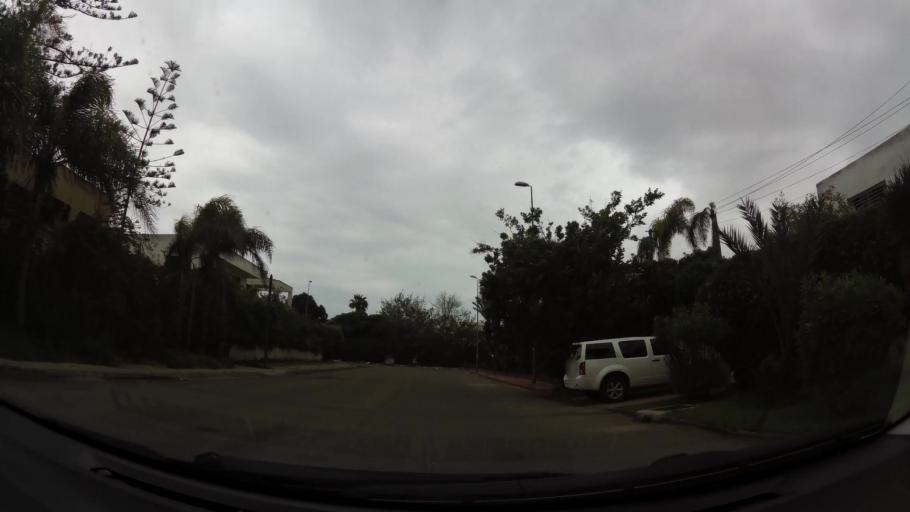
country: MA
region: Grand Casablanca
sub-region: Casablanca
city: Casablanca
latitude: 33.5773
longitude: -7.6665
